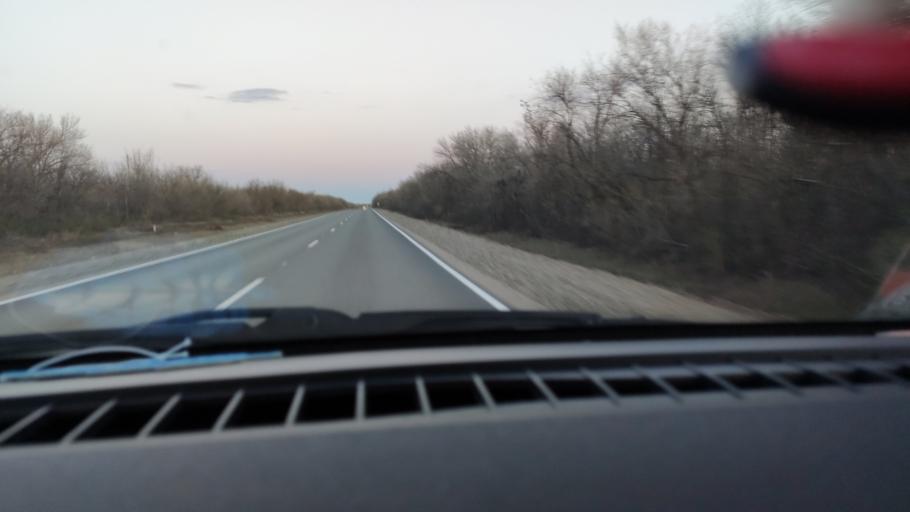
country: RU
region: Saratov
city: Privolzhskiy
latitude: 51.1662
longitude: 45.9463
